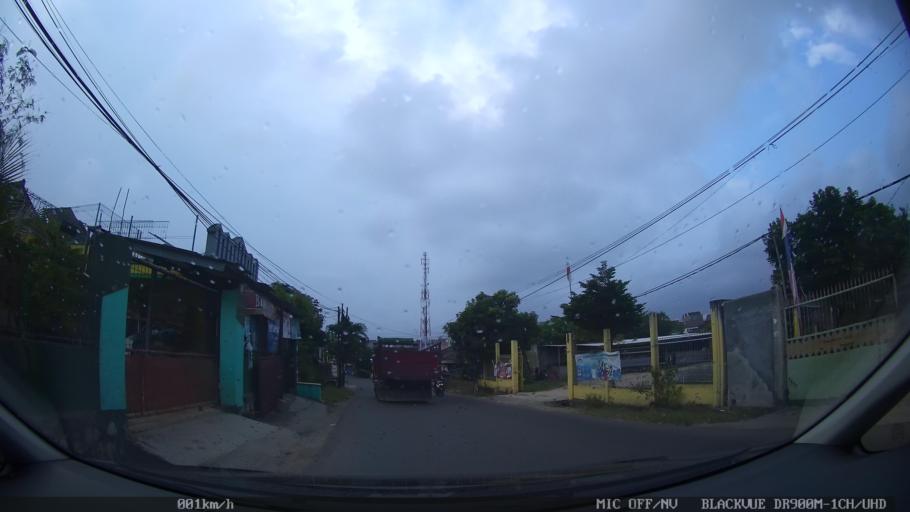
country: ID
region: Lampung
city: Bandarlampung
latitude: -5.4174
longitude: 105.2859
